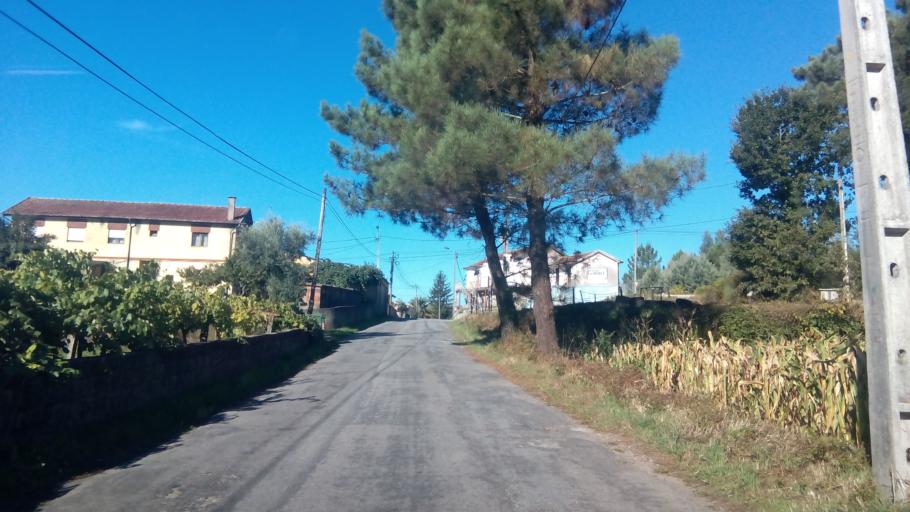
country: PT
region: Porto
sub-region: Paredes
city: Gandra
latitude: 41.1912
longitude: -8.4462
